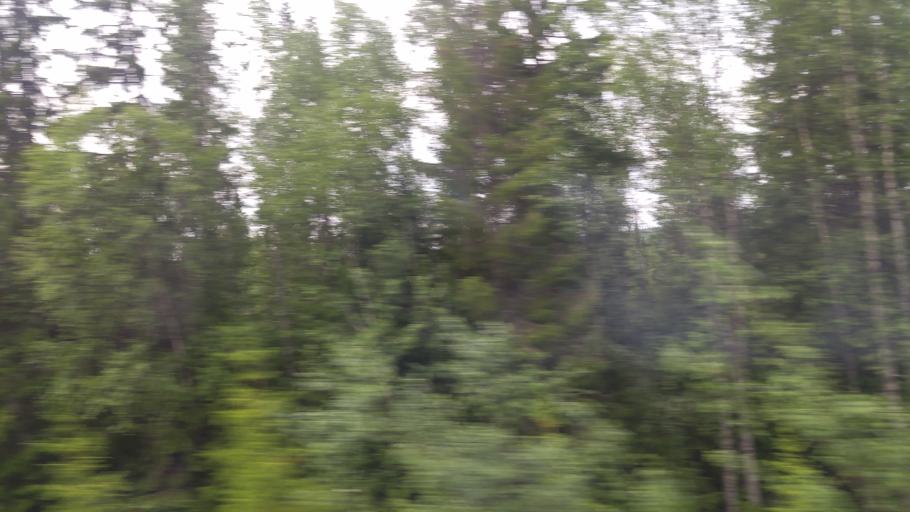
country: SE
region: Jaemtland
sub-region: Are Kommun
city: Are
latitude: 63.3959
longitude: 12.8217
